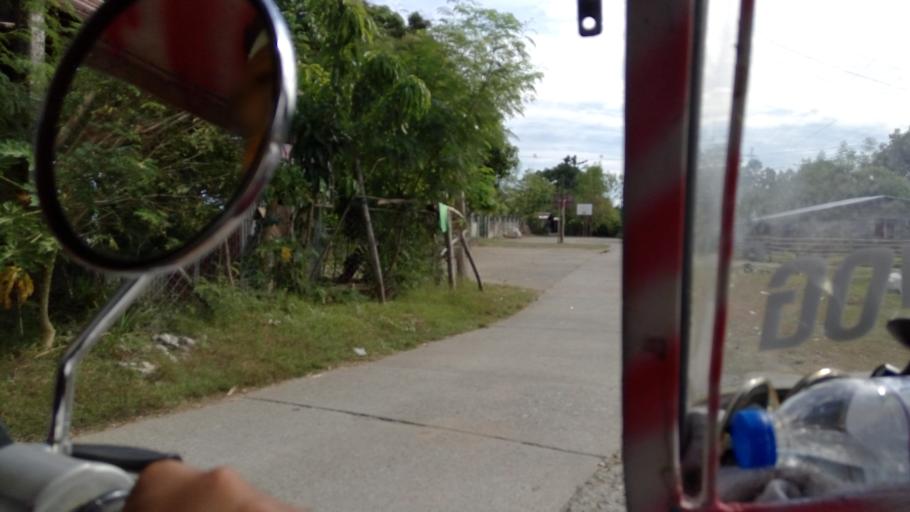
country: PH
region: Ilocos
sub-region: Province of La Union
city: San Eugenio
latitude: 16.3750
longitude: 120.3523
